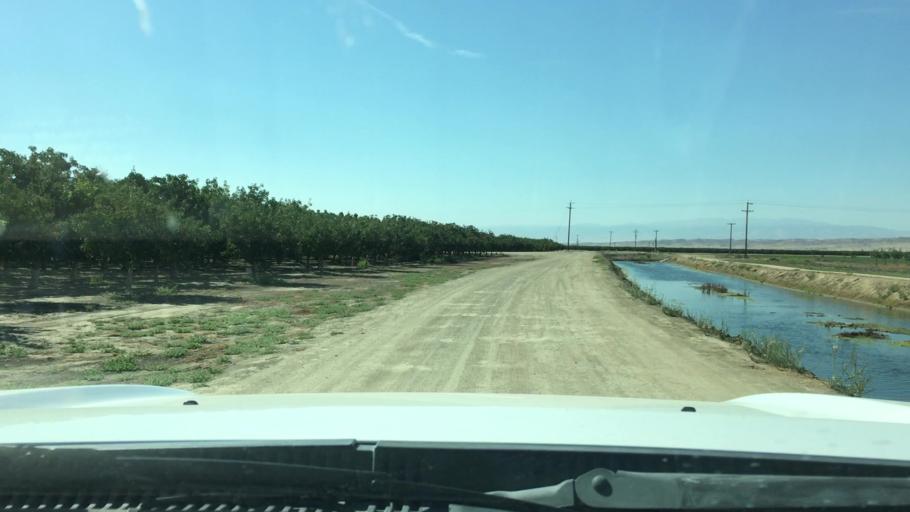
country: US
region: California
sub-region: Kern County
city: Buttonwillow
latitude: 35.3710
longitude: -119.3998
